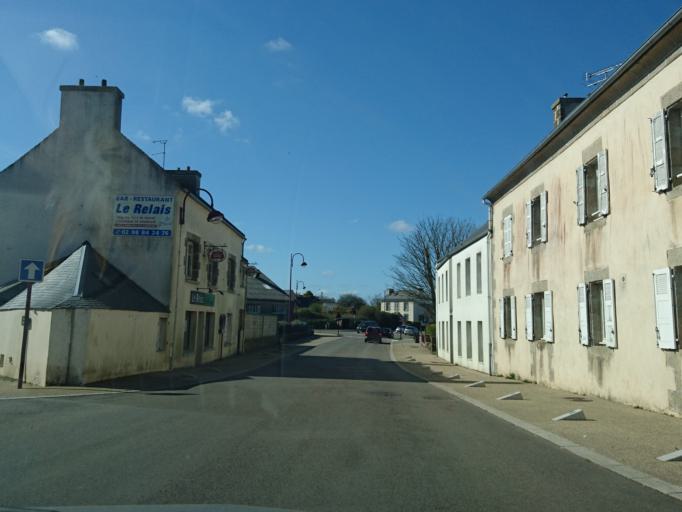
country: FR
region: Brittany
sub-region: Departement du Finistere
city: Lanrivoare
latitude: 48.4735
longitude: -4.6398
